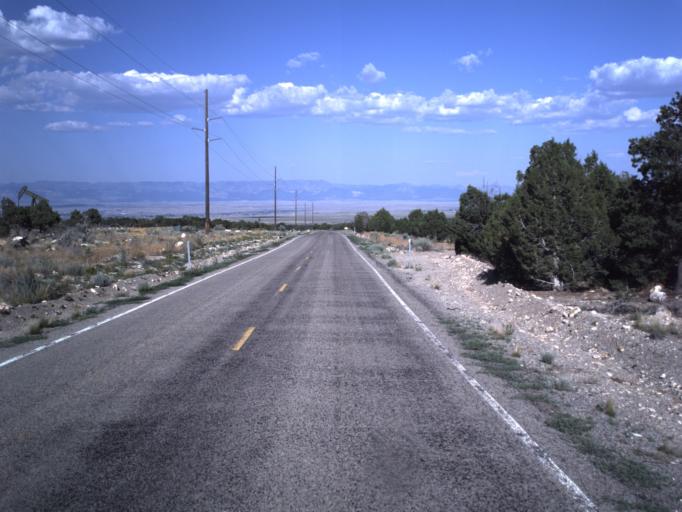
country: US
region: Utah
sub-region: Emery County
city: Huntington
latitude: 39.4869
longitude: -110.9438
